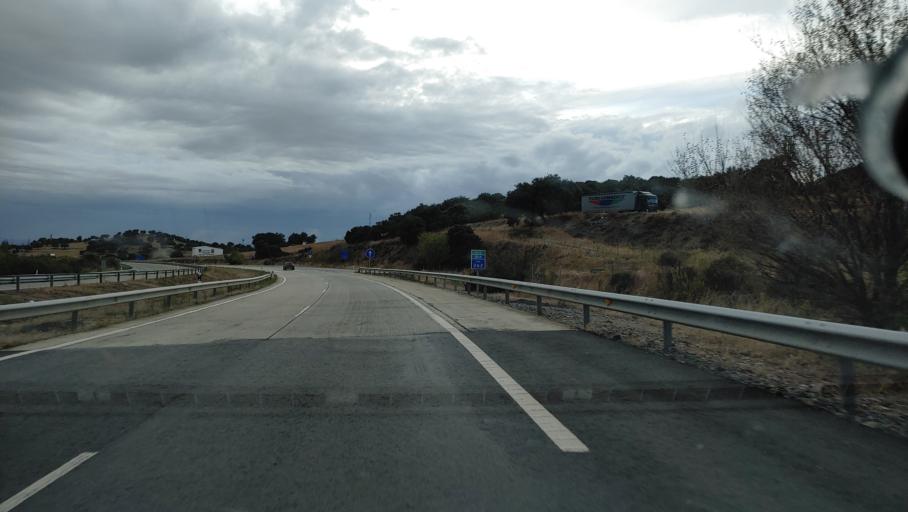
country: ES
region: Andalusia
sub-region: Provincia de Jaen
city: Santa Elena
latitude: 38.3135
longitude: -3.5708
